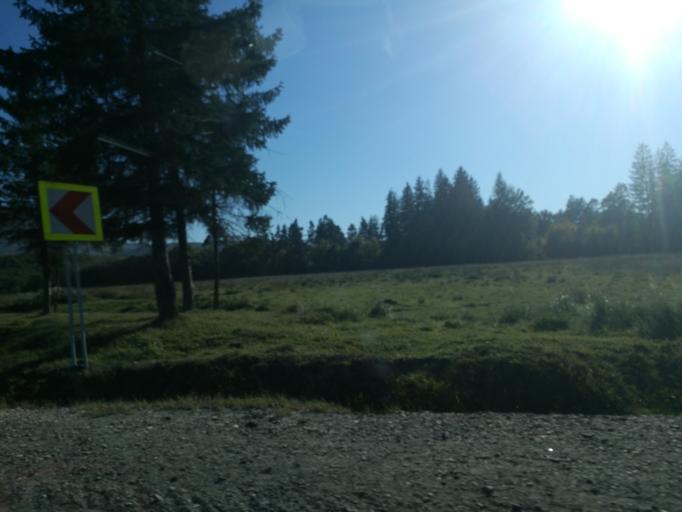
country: RO
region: Brasov
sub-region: Comuna Dumbravita
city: Dumbravita
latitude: 45.7583
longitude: 25.3871
